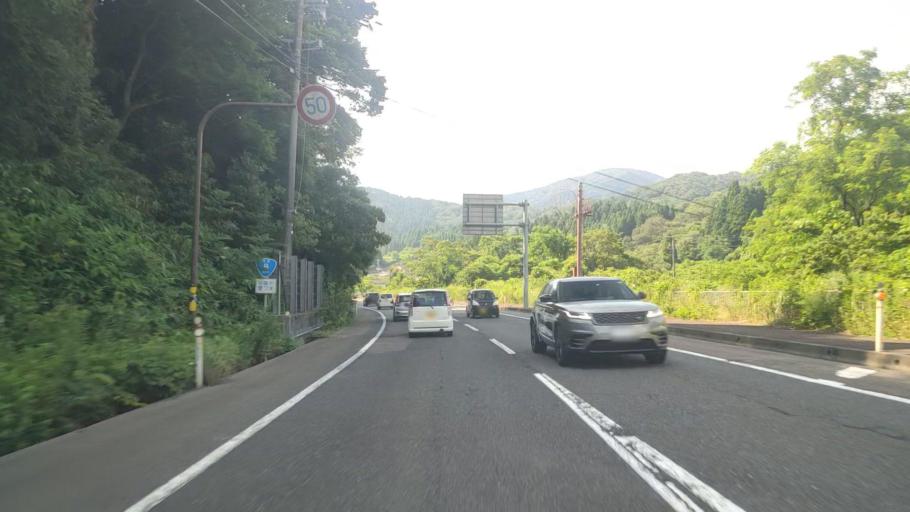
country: JP
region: Fukui
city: Tsuruga
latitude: 35.6075
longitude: 136.1208
